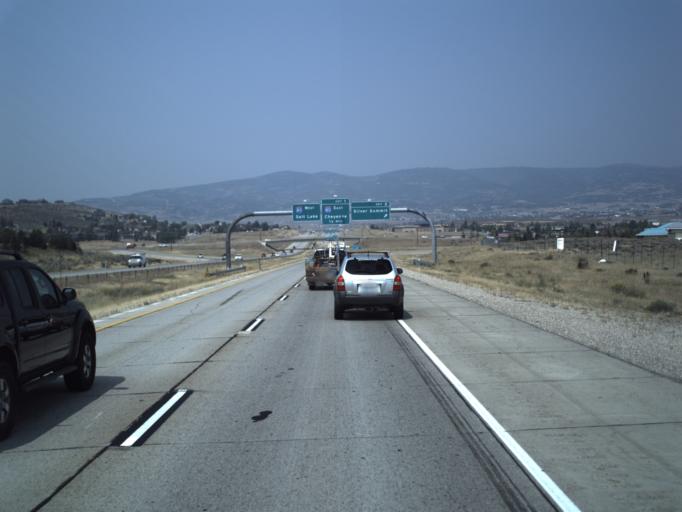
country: US
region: Utah
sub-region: Summit County
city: Snyderville
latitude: 40.7127
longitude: -111.4828
